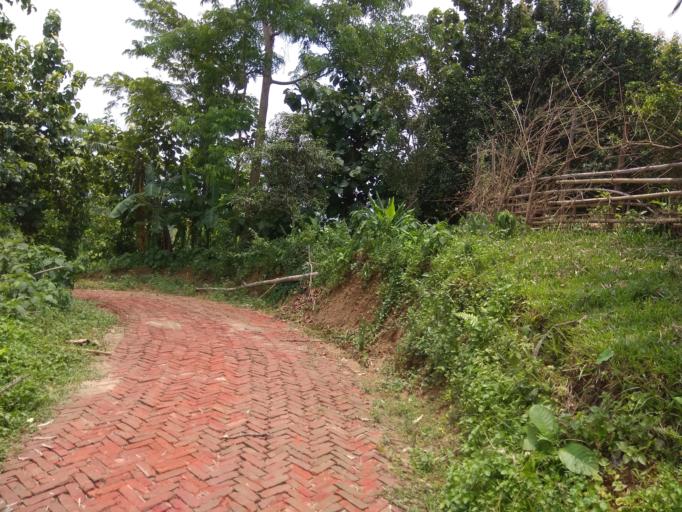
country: BD
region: Chittagong
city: Manikchari
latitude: 22.8841
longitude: 91.9261
